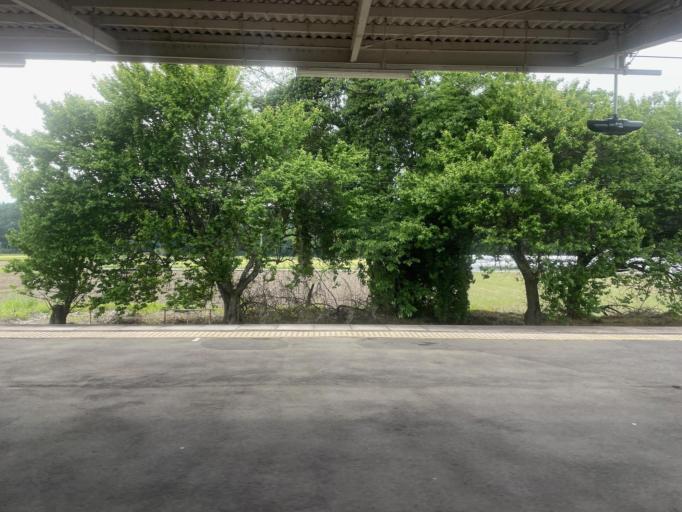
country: JP
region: Tochigi
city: Kanuma
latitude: 36.5075
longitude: 139.7452
